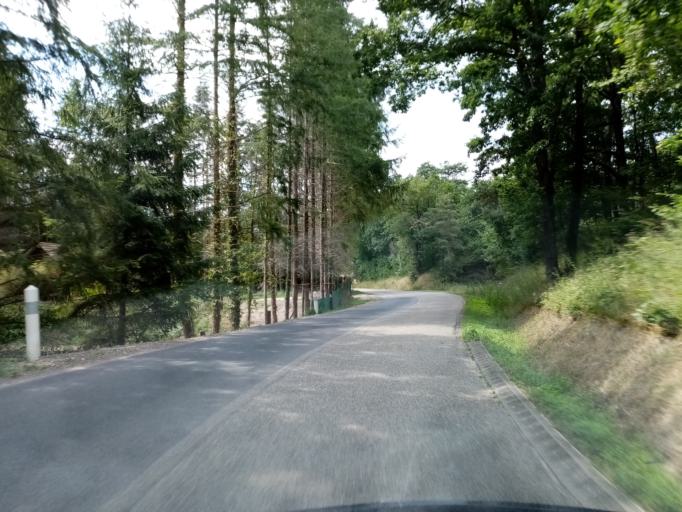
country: FR
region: Alsace
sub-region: Departement du Bas-Rhin
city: Dambach-la-Ville
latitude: 48.3302
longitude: 7.3735
